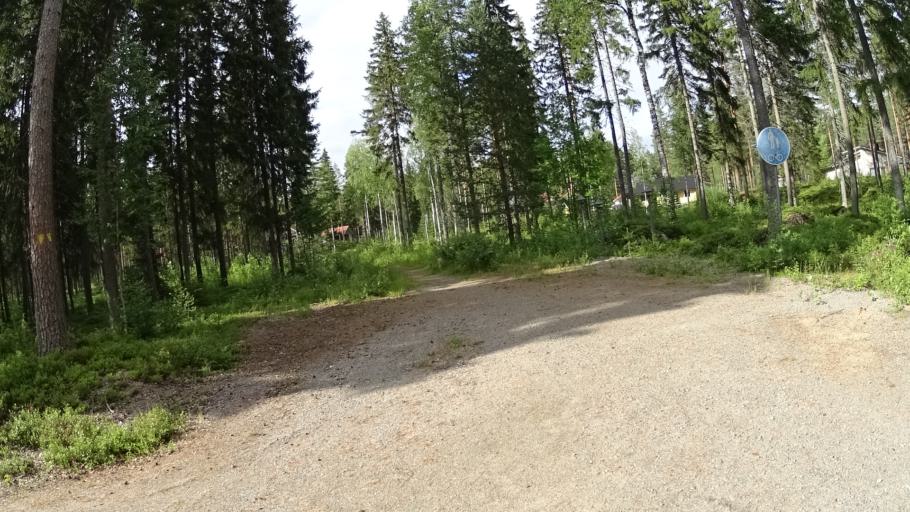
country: FI
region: Southern Ostrobothnia
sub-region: Kuusiokunnat
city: AEhtaeri
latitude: 62.5284
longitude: 24.1937
